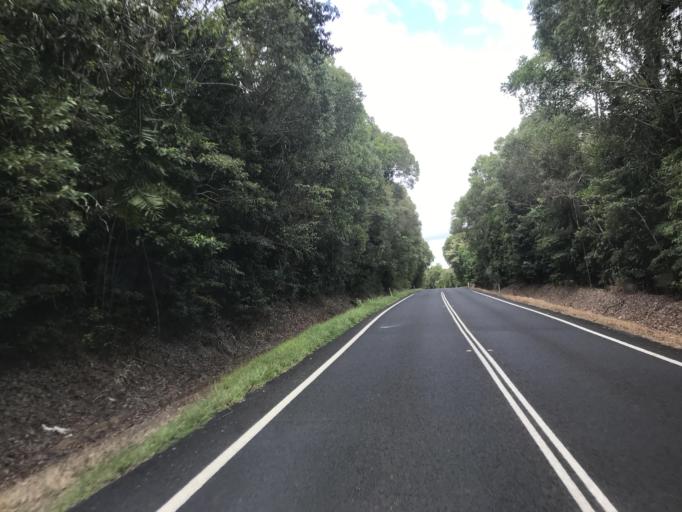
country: AU
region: Queensland
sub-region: Cassowary Coast
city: Innisfail
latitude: -17.8145
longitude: 146.0334
